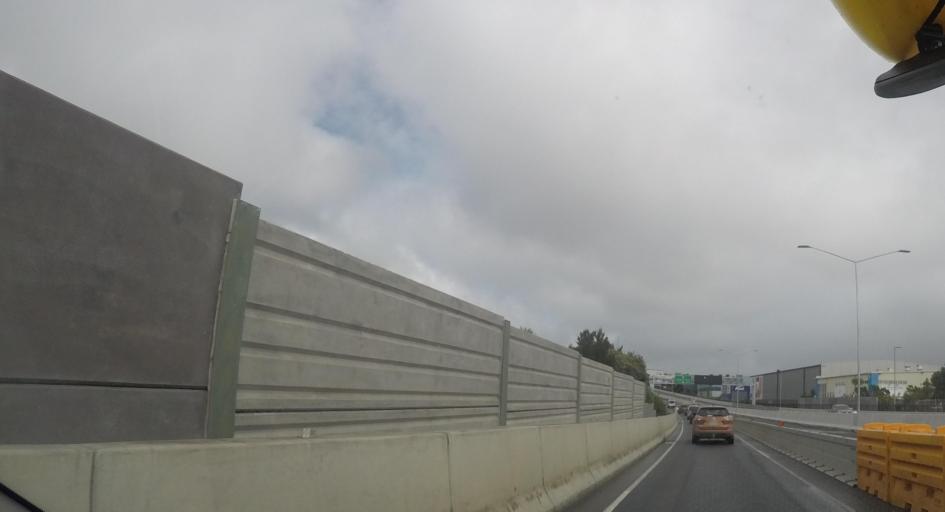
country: NZ
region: Auckland
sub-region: Auckland
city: Rothesay Bay
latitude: -36.7531
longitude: 174.7126
